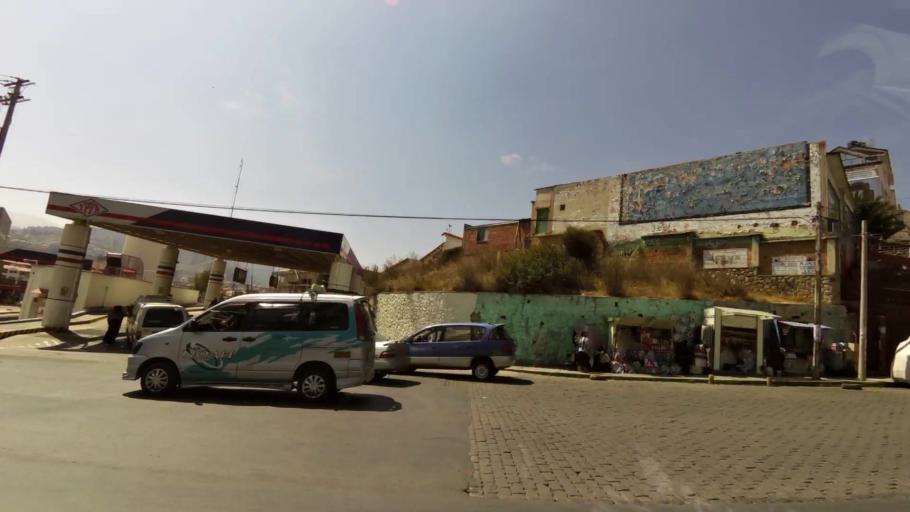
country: BO
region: La Paz
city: La Paz
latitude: -16.5397
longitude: -68.0751
